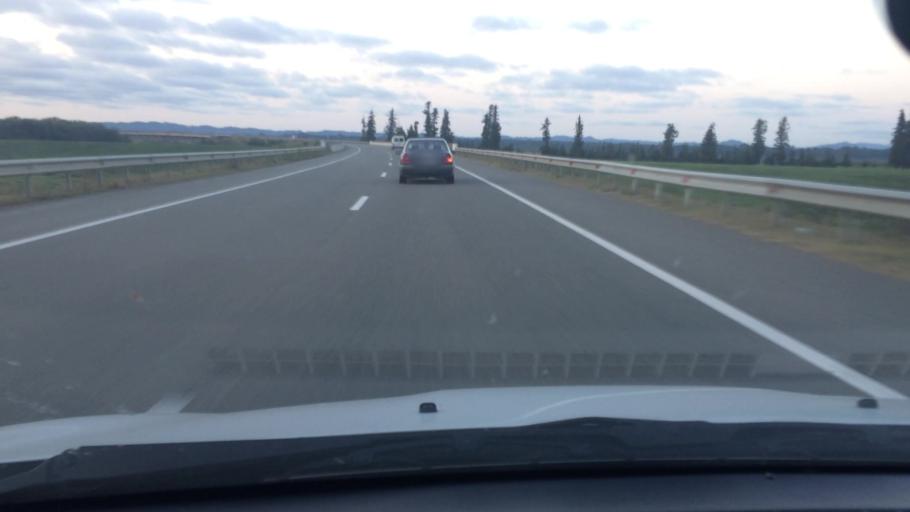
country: GE
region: Ajaria
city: Ochkhamuri
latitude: 41.8582
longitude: 41.8384
